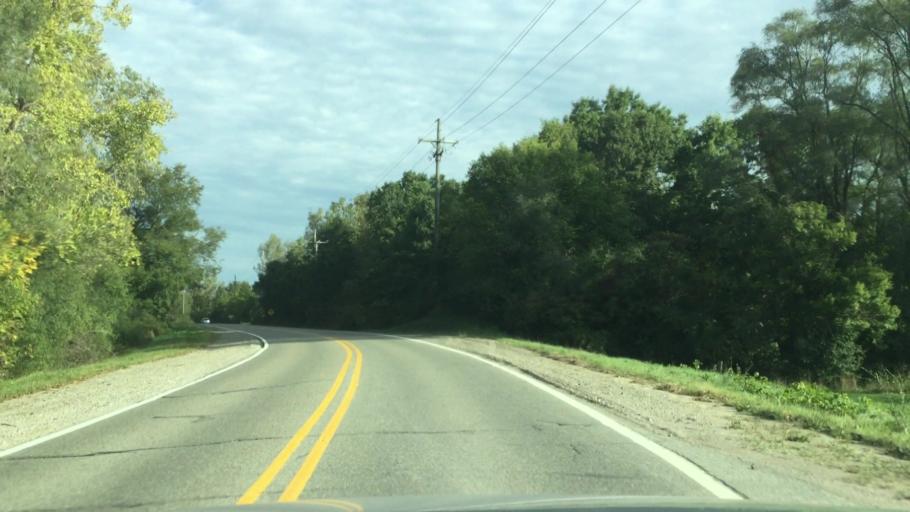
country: US
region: Michigan
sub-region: Livingston County
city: Brighton
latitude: 42.5177
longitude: -83.8552
